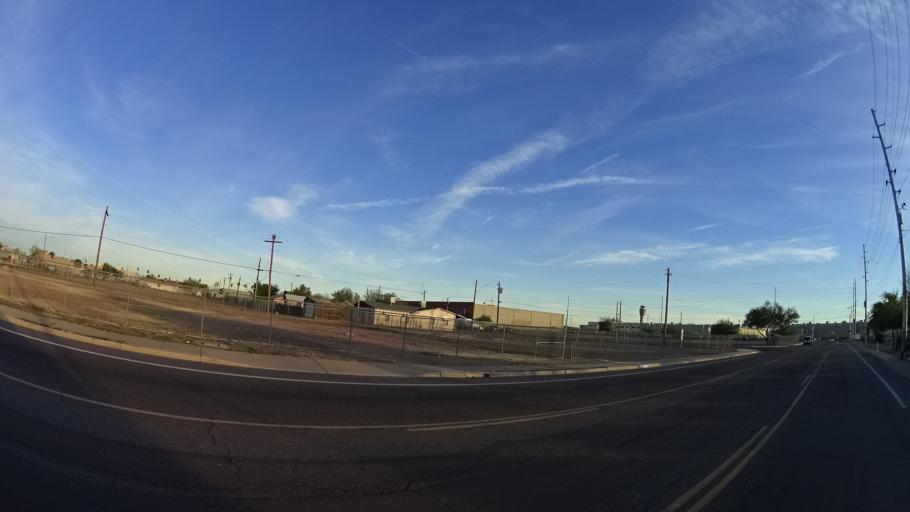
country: US
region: Arizona
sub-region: Maricopa County
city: Phoenix
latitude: 33.4459
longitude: -112.0130
